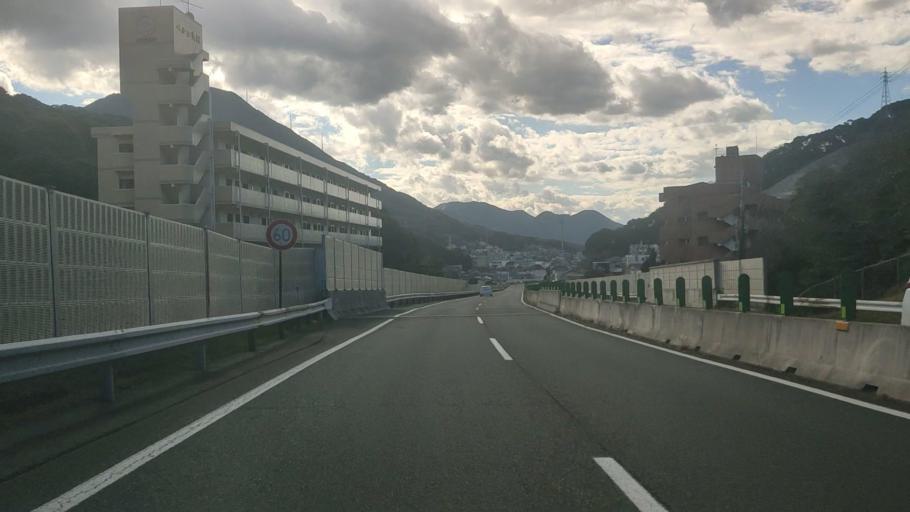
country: JP
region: Yamaguchi
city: Shimonoseki
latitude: 33.9132
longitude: 130.9600
